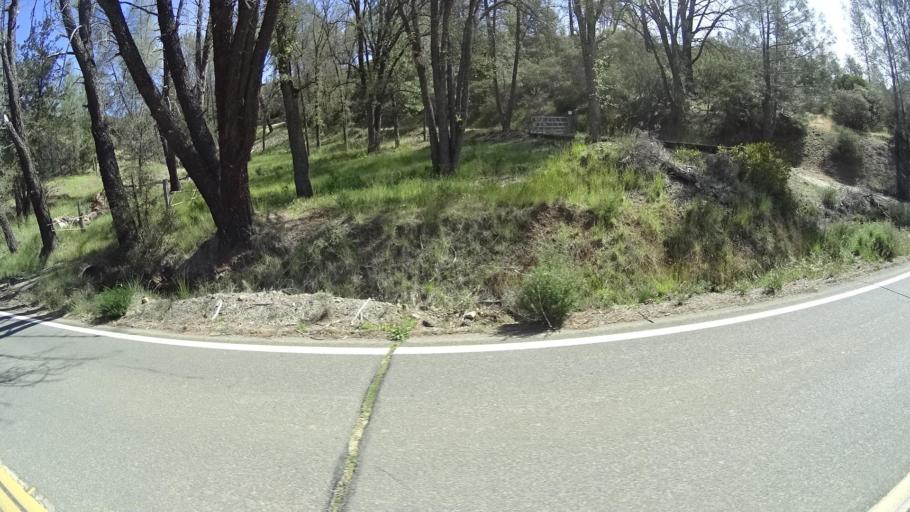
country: US
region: California
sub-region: Lake County
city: Cobb
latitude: 38.8618
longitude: -122.7634
